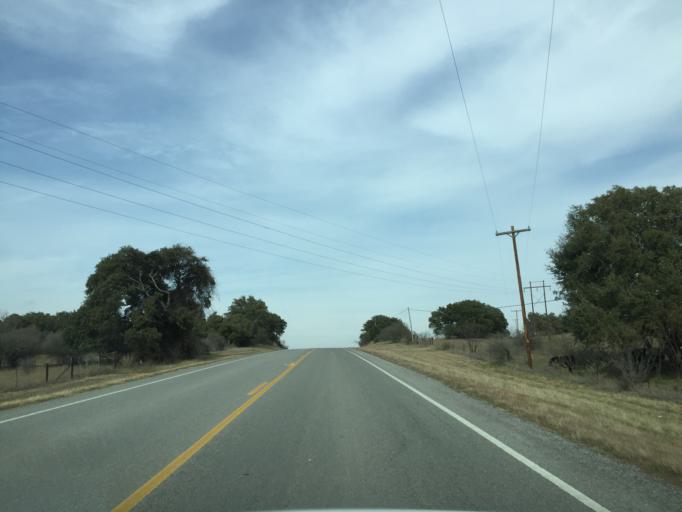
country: US
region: Texas
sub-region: Gillespie County
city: Fredericksburg
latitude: 30.4472
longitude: -98.7337
